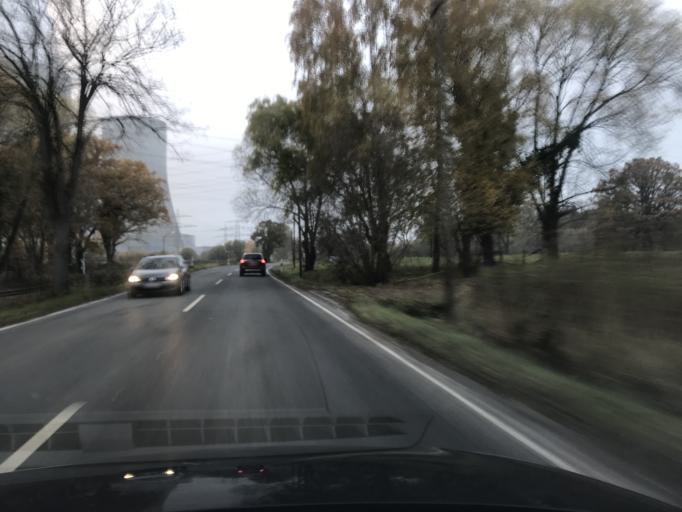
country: DE
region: North Rhine-Westphalia
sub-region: Regierungsbezirk Arnsberg
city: Welver
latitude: 51.6747
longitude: 7.9834
